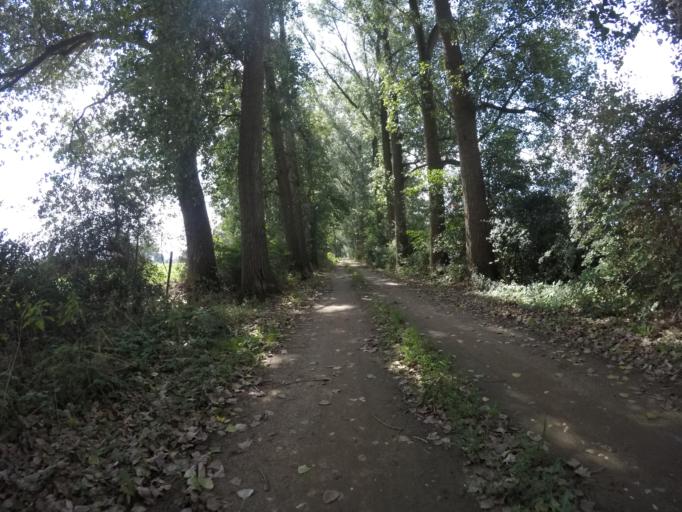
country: DE
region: North Rhine-Westphalia
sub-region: Regierungsbezirk Munster
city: Isselburg
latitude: 51.8020
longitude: 6.4711
